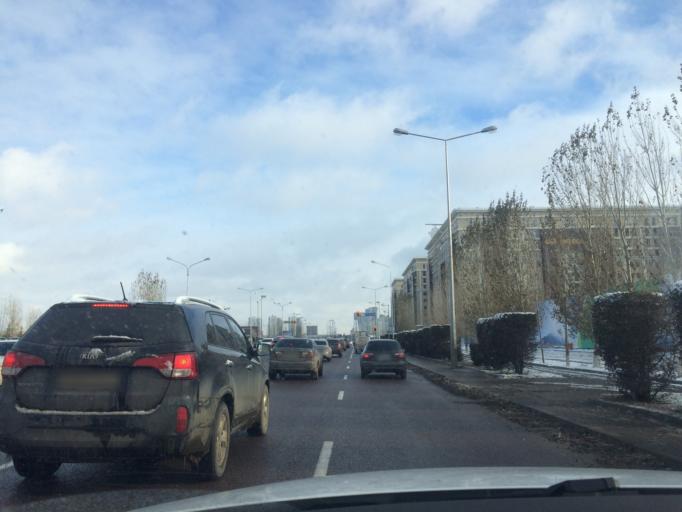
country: KZ
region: Astana Qalasy
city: Astana
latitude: 51.1336
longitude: 71.4324
